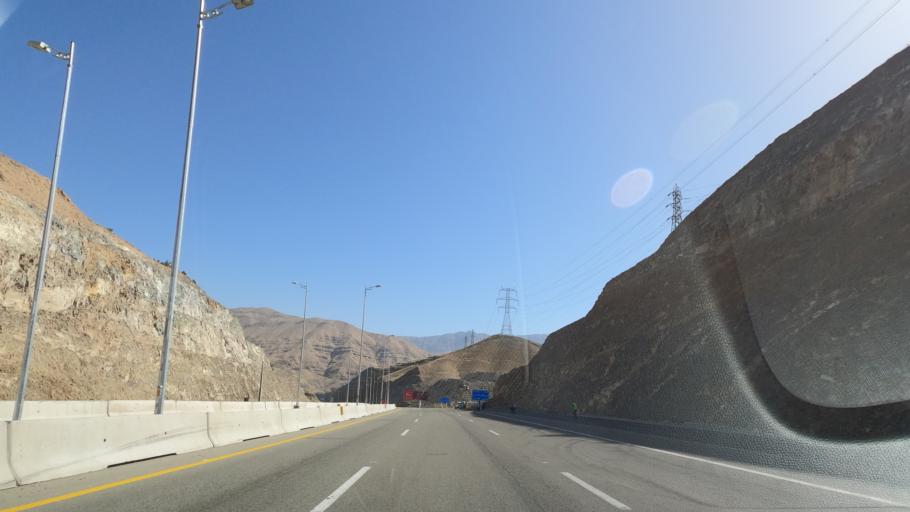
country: IR
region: Alborz
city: Karaj
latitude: 35.8136
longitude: 51.0370
